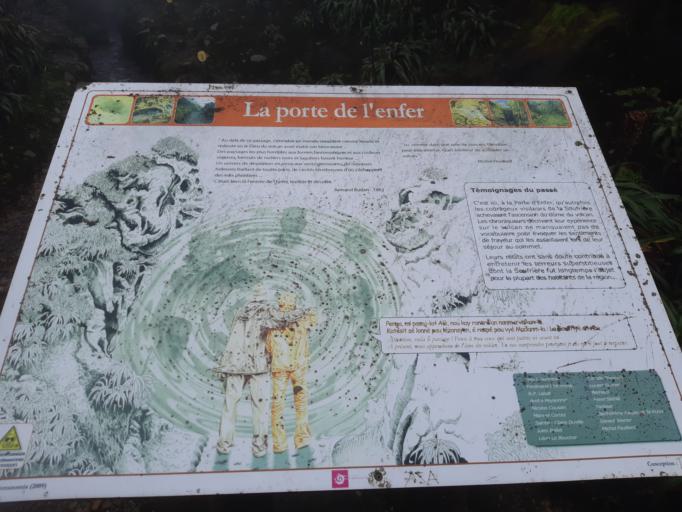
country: GP
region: Guadeloupe
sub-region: Guadeloupe
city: Saint-Claude
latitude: 16.0439
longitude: -61.6644
